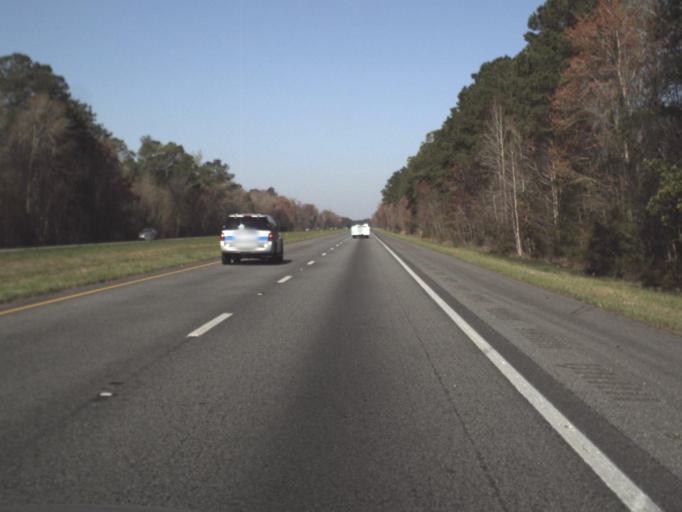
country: US
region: Florida
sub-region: Jefferson County
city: Monticello
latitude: 30.4637
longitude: -83.7910
